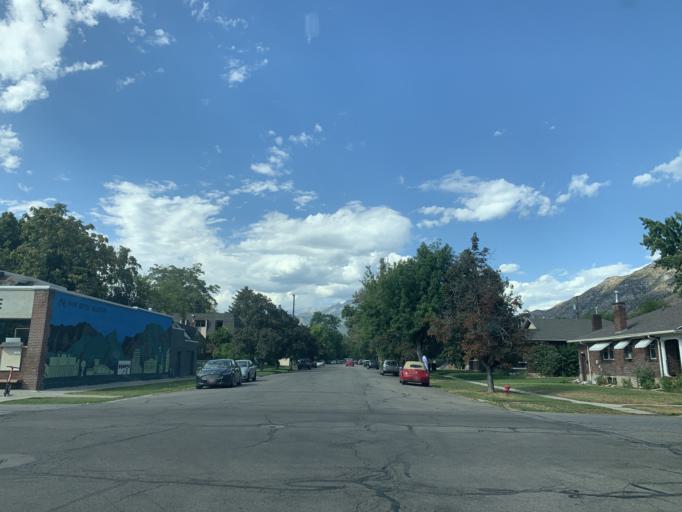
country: US
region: Utah
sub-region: Utah County
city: Provo
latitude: 40.2364
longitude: -111.6516
